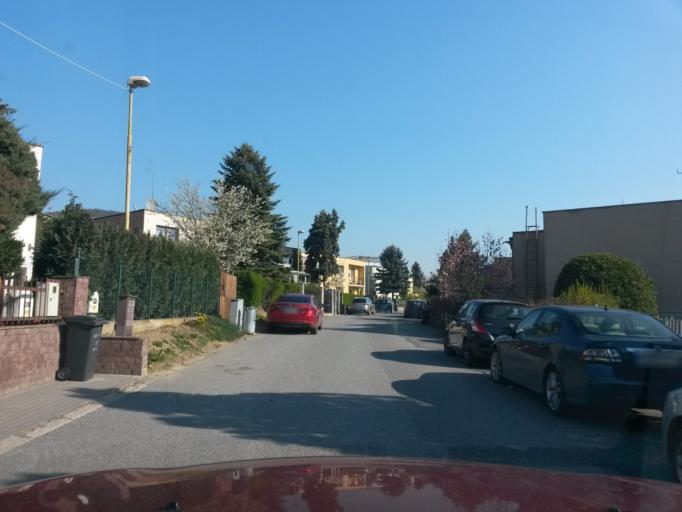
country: SK
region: Kosicky
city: Kosice
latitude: 48.7494
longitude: 21.2452
